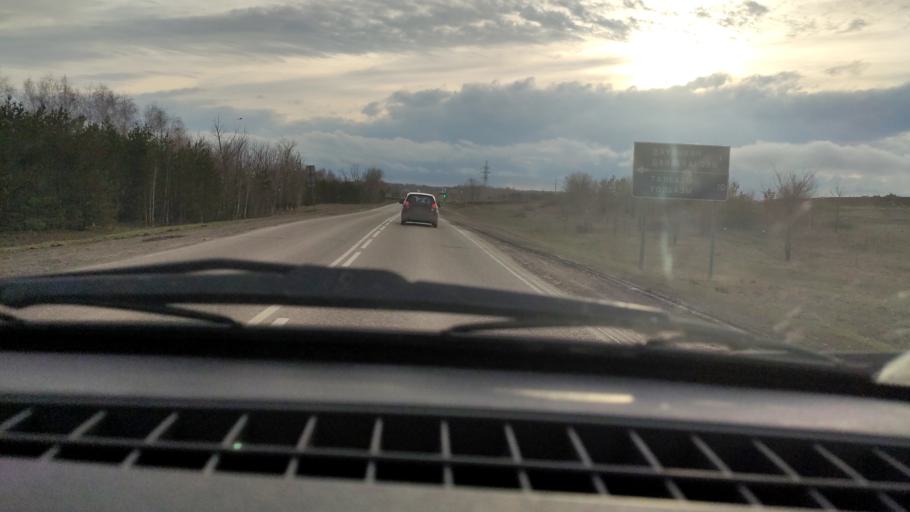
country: RU
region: Bashkortostan
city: Davlekanovo
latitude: 54.2394
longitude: 55.0544
